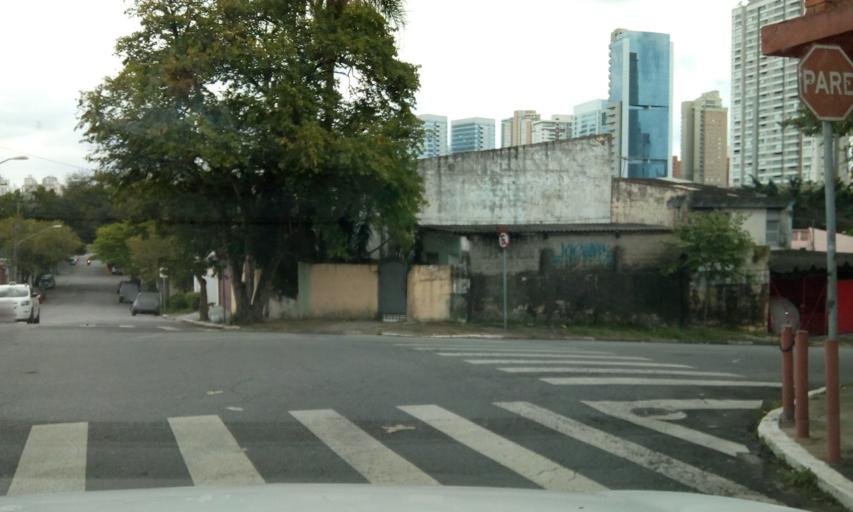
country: BR
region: Sao Paulo
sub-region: Sao Paulo
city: Sao Paulo
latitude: -23.6168
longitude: -46.6906
